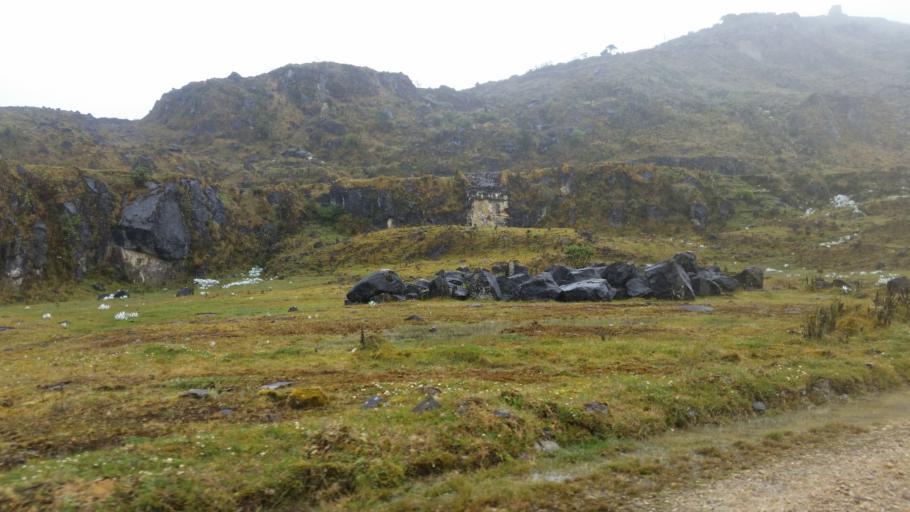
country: CO
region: Cundinamarca
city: La Calera
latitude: 4.7189
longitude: -73.8205
